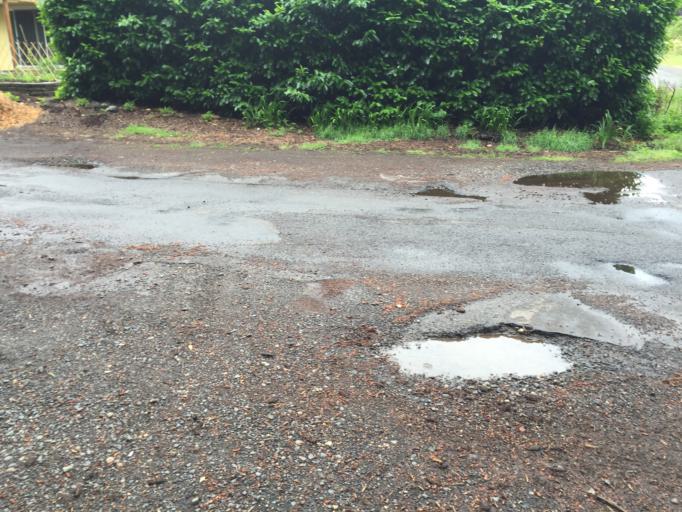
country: US
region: Oregon
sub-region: Multnomah County
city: Lents
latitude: 45.5321
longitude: -122.6075
